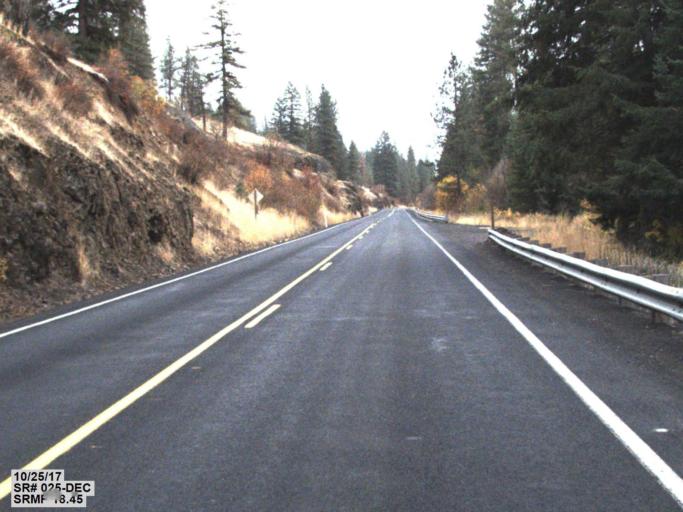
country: US
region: Washington
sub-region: Lincoln County
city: Davenport
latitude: 47.8738
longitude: -118.2660
